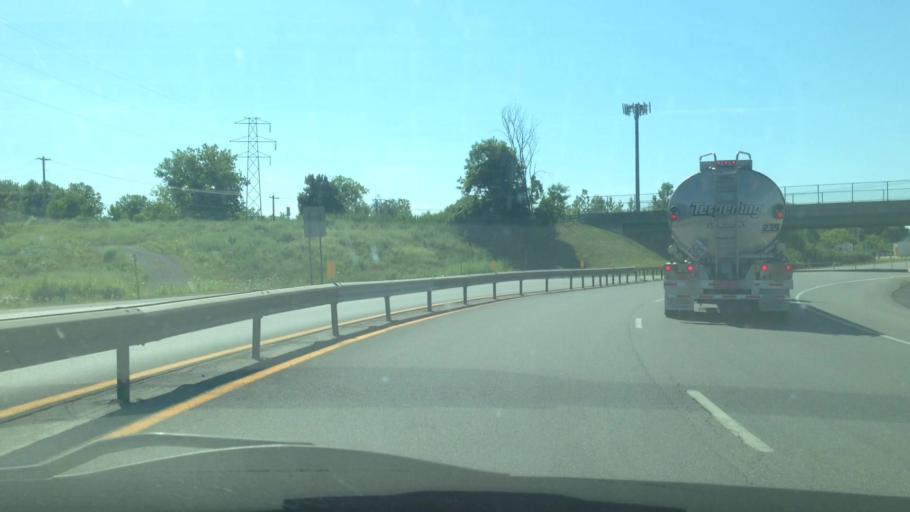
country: US
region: New York
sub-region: Oneida County
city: Utica
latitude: 43.1106
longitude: -75.2075
